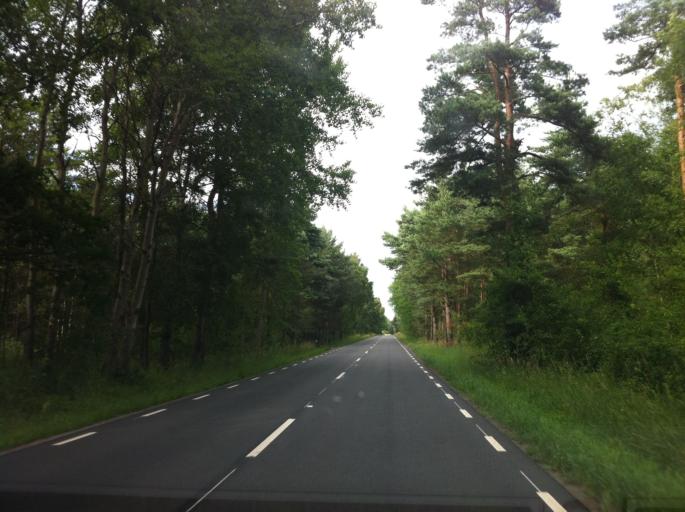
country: SE
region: Skane
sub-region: Ystads Kommun
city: Kopingebro
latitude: 55.3957
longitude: 14.1568
